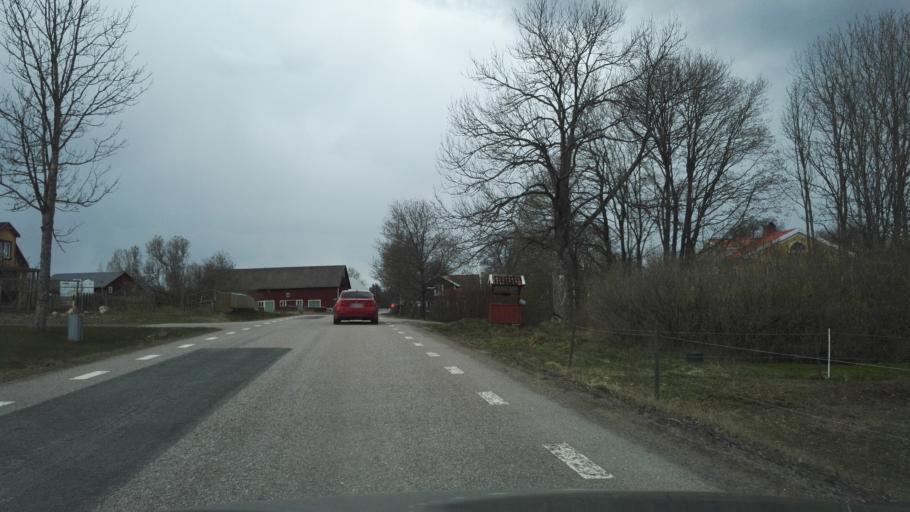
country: SE
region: Kronoberg
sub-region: Vaxjo Kommun
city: Braas
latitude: 57.1105
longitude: 14.9787
